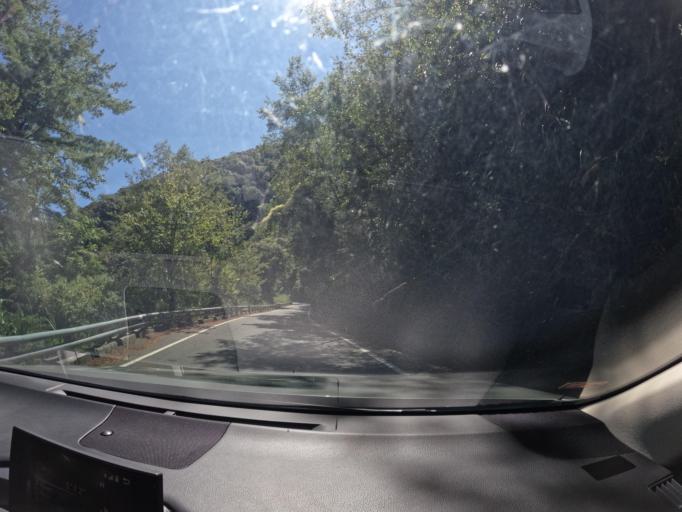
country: TW
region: Taiwan
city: Yujing
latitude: 23.2860
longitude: 120.8993
